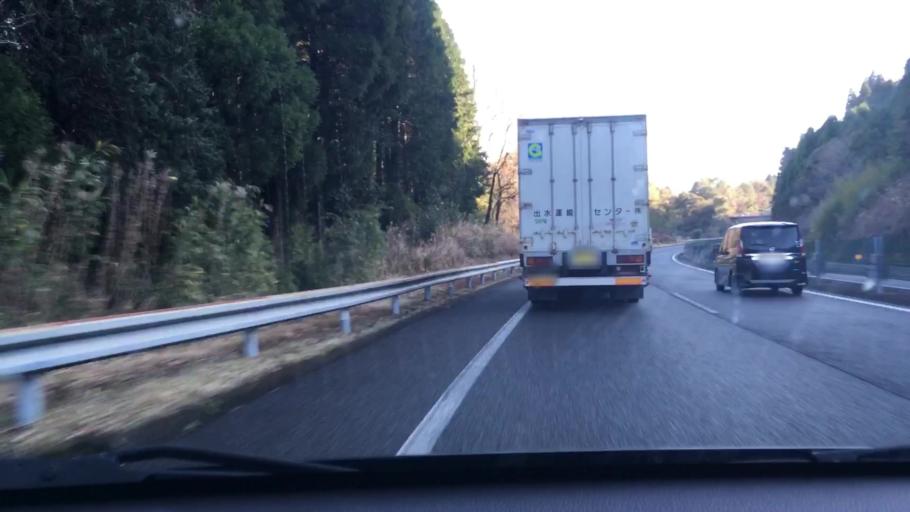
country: JP
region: Kagoshima
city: Kajiki
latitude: 31.8315
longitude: 130.6929
